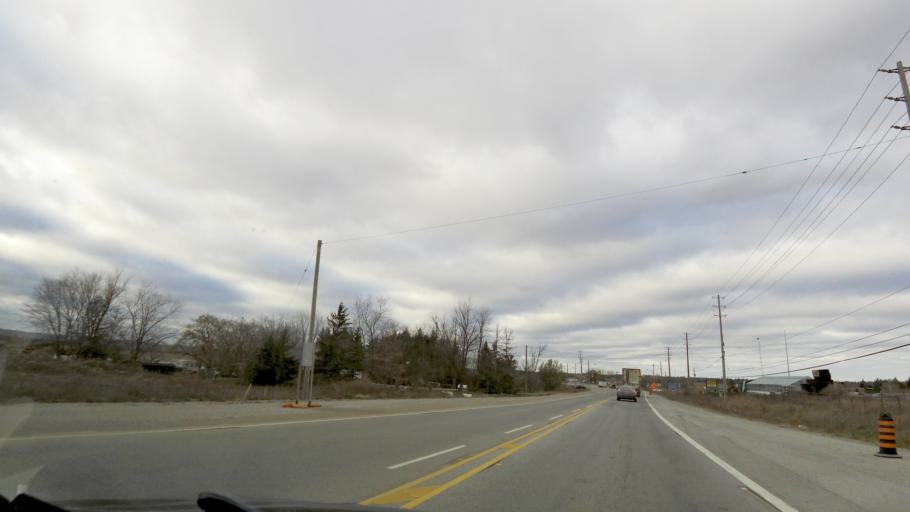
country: CA
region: Ontario
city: Burlington
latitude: 43.4648
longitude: -79.8072
